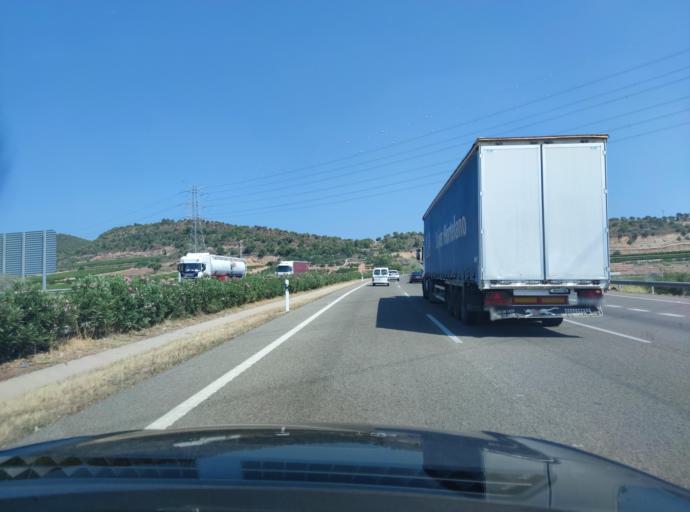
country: ES
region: Valencia
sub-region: Provincia de Valencia
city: Petres
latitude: 39.6549
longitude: -0.3045
